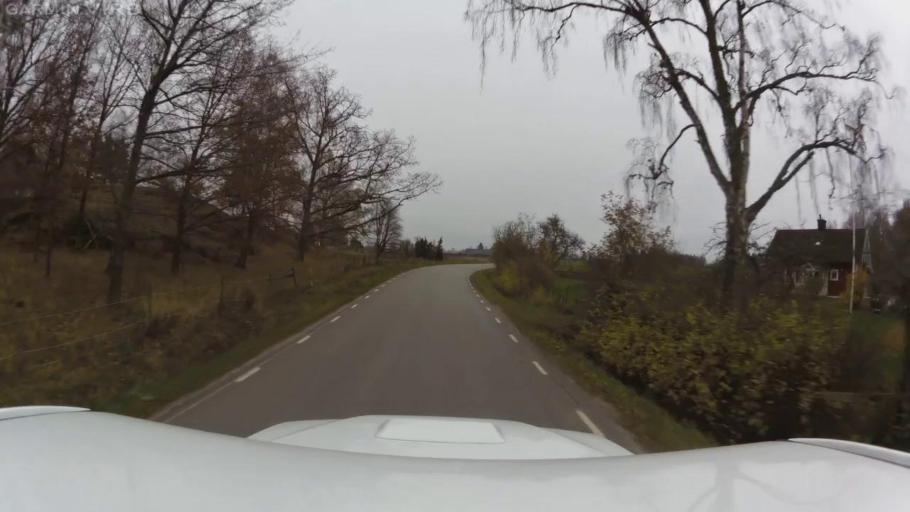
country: SE
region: OEstergoetland
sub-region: Linkopings Kommun
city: Vikingstad
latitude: 58.3137
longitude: 15.3756
